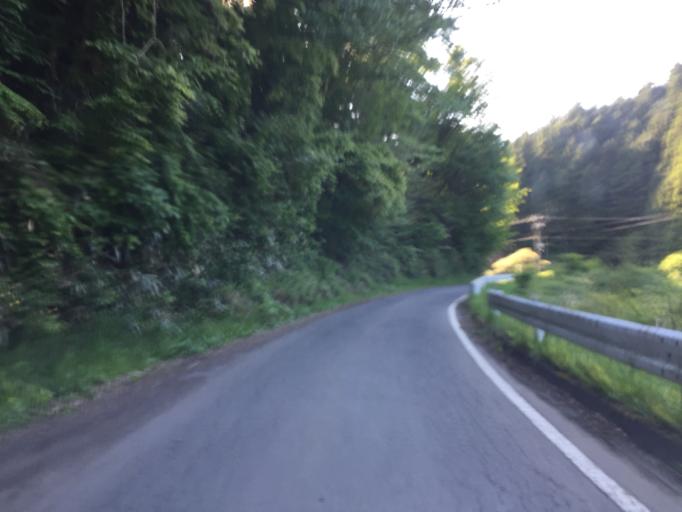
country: JP
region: Ibaraki
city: Kitaibaraki
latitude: 36.9210
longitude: 140.5510
